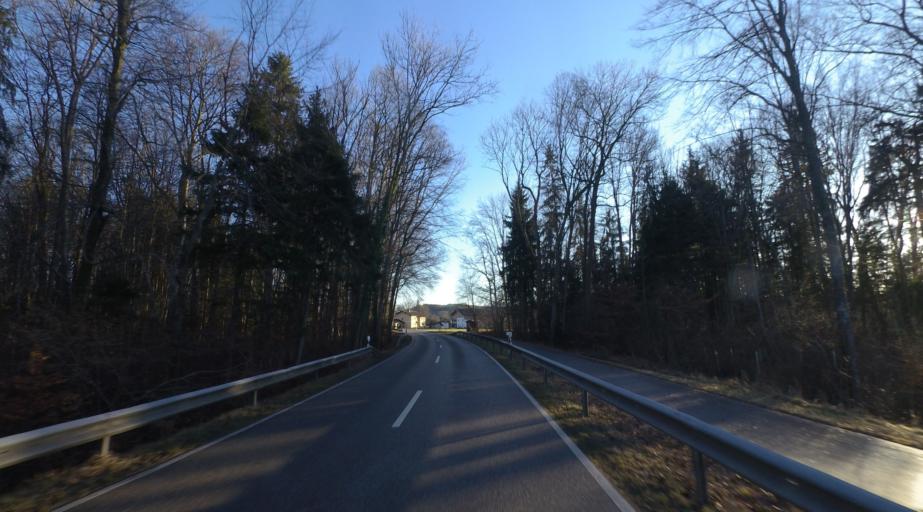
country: DE
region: Bavaria
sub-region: Upper Bavaria
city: Kirchanschoring
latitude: 47.9665
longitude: 12.8219
